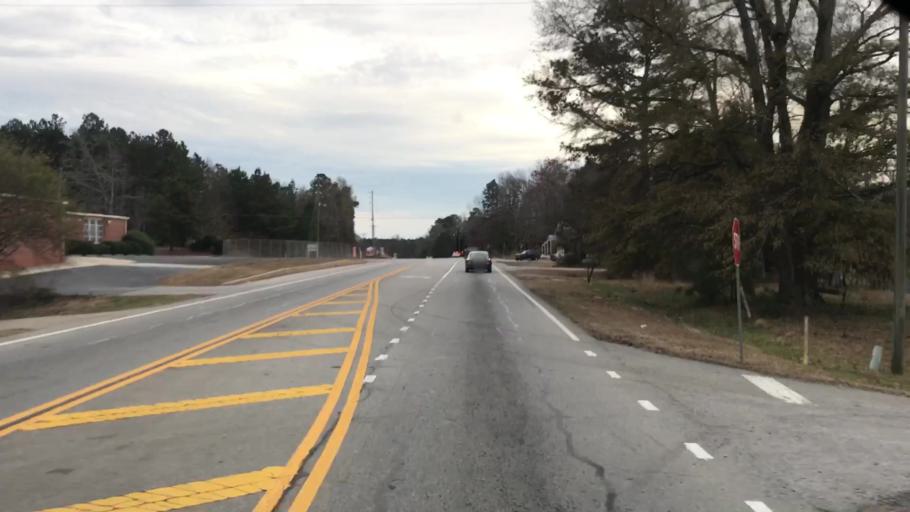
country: US
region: Georgia
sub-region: Jackson County
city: Hoschton
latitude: 34.0448
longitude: -83.7771
